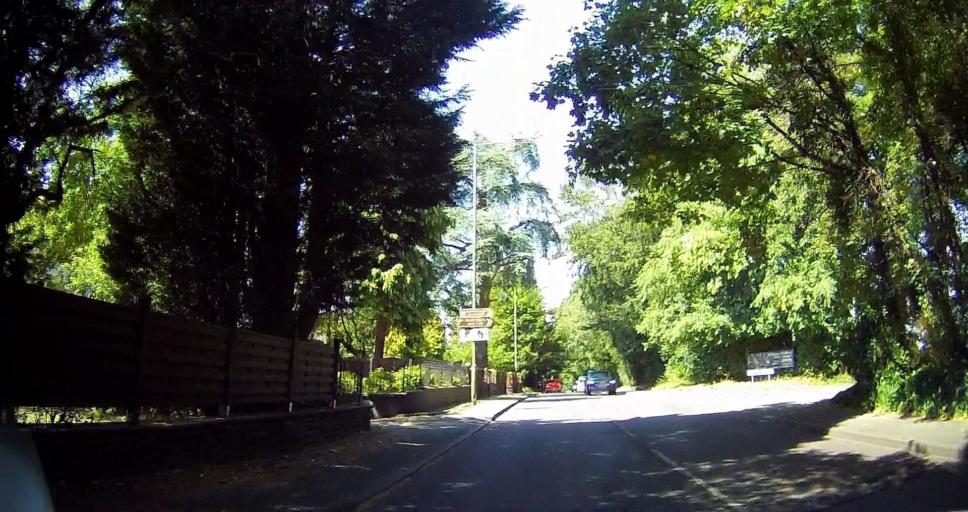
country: GB
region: England
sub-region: Staffordshire
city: Codsall
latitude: 52.6016
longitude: -2.1746
